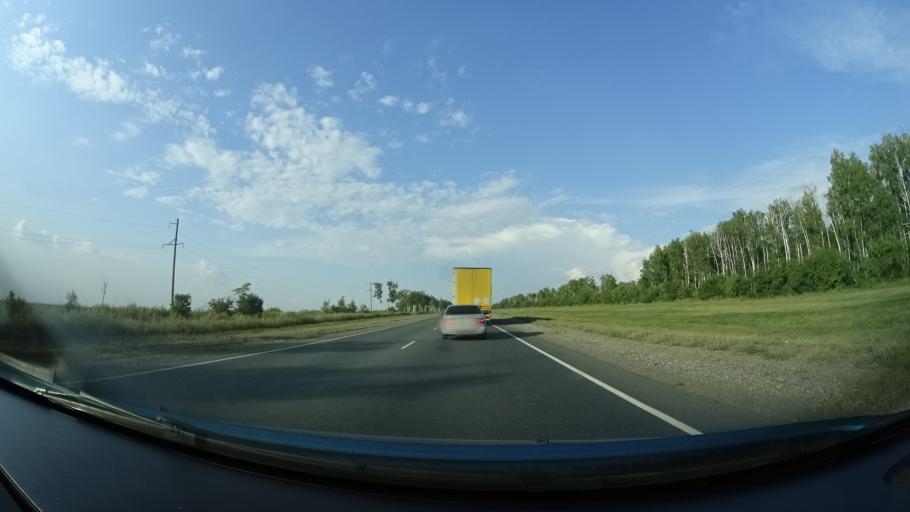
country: RU
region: Samara
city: Krasnyy Yar
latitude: 53.6610
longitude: 50.7546
